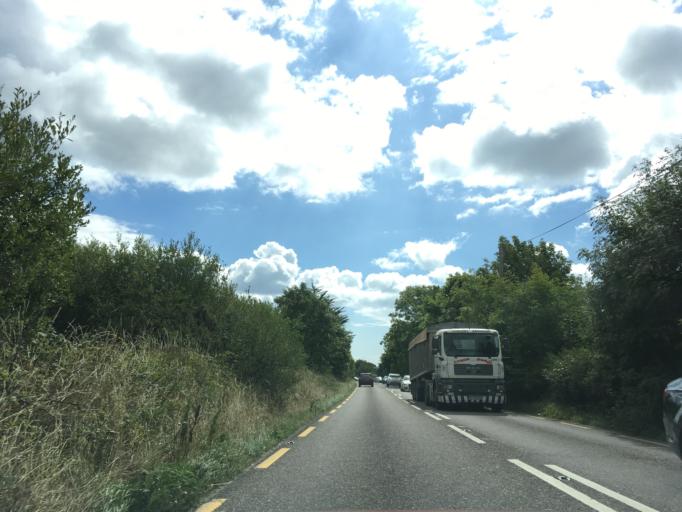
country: IE
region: Munster
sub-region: County Cork
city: Carrigaline
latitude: 51.8475
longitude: -8.4087
